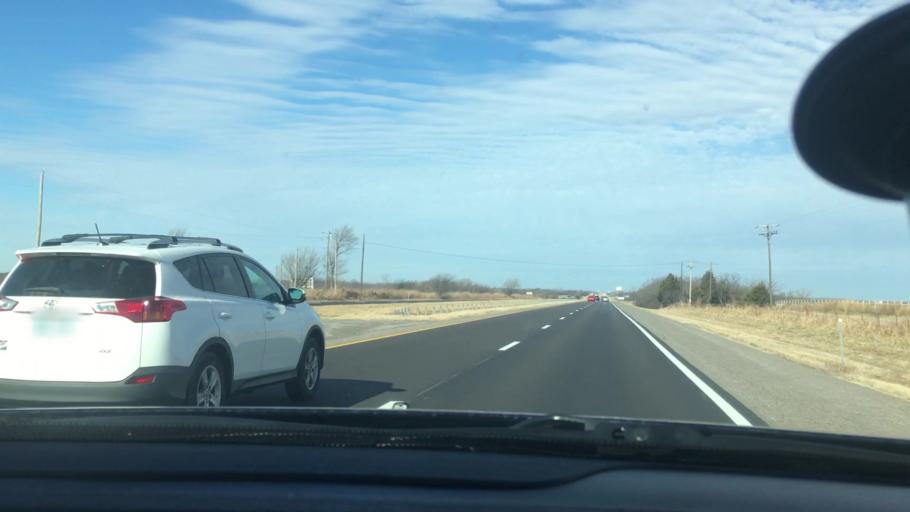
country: US
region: Oklahoma
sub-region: Cleveland County
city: Noble
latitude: 35.0949
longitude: -97.4227
